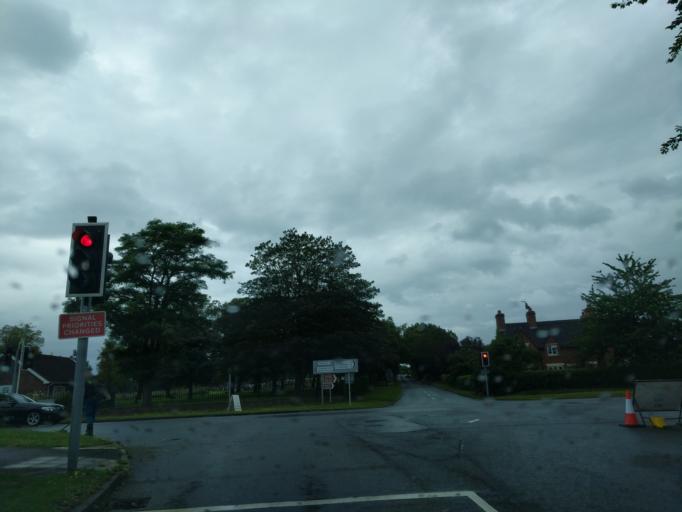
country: GB
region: England
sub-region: Staffordshire
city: Stafford
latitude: 52.8077
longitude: -2.0742
